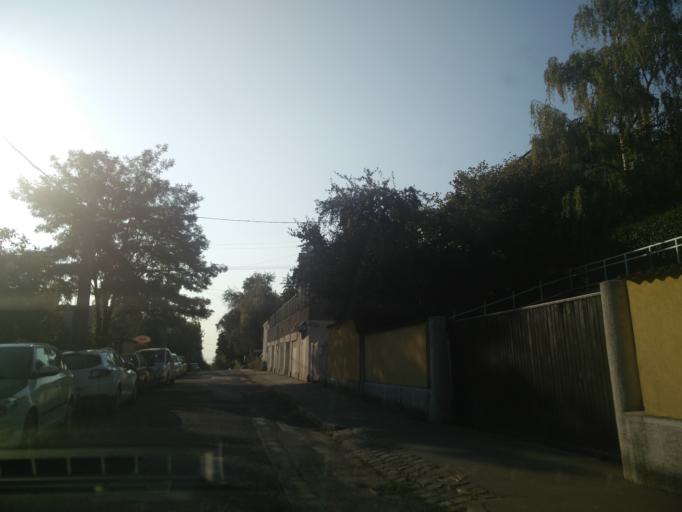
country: HU
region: Budapest
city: Budapest XII. keruelet
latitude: 47.5058
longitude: 18.9988
